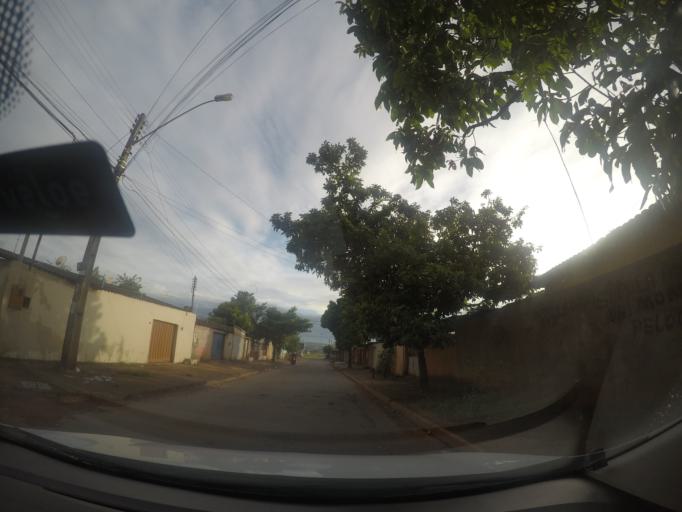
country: BR
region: Goias
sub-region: Goiania
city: Goiania
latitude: -16.6426
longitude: -49.3202
